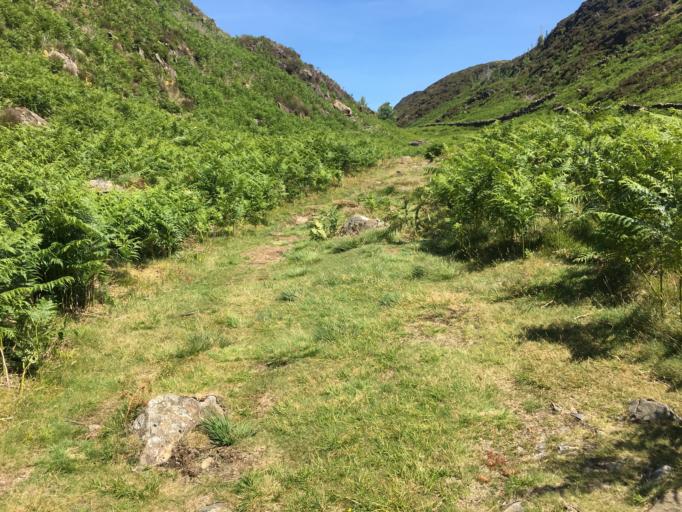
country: GB
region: Wales
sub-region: Gwynedd
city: Penrhyndeudraeth
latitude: 53.0025
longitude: -4.0852
